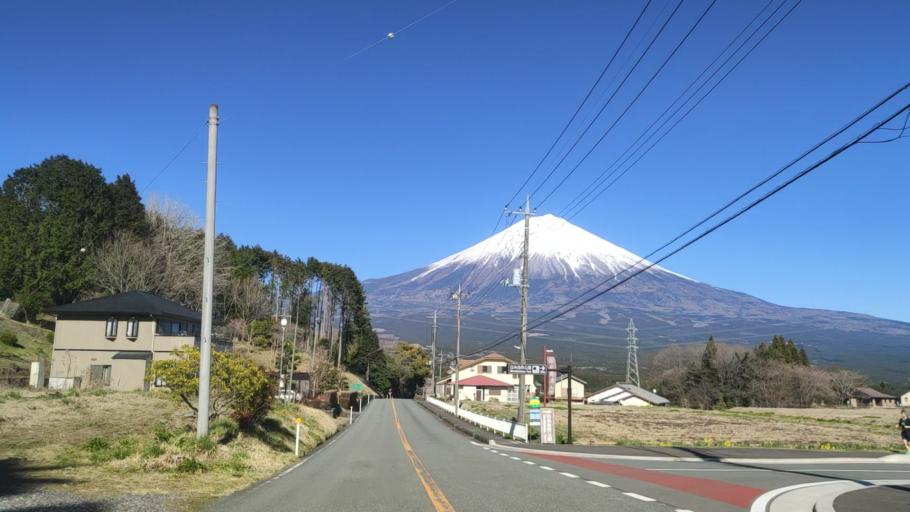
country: JP
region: Shizuoka
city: Fujinomiya
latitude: 35.3109
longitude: 138.5820
